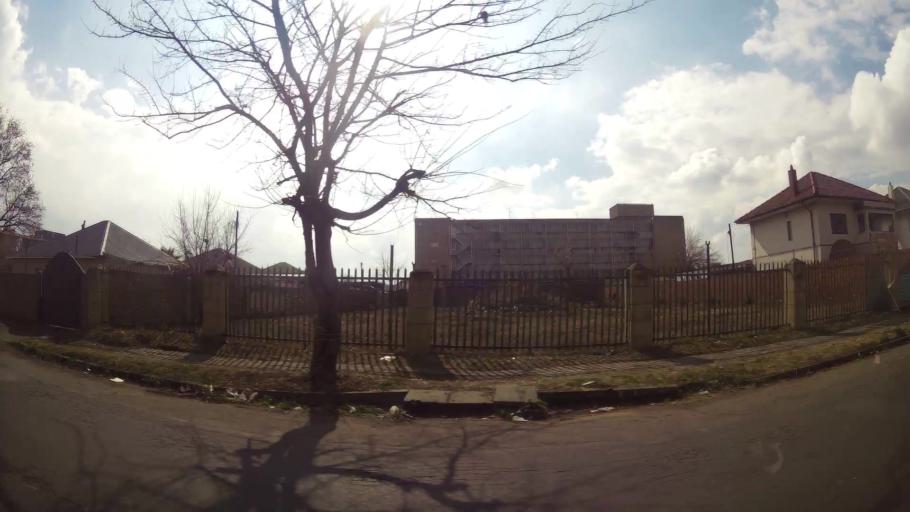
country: ZA
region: Gauteng
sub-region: Sedibeng District Municipality
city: Vereeniging
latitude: -26.6753
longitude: 27.9256
